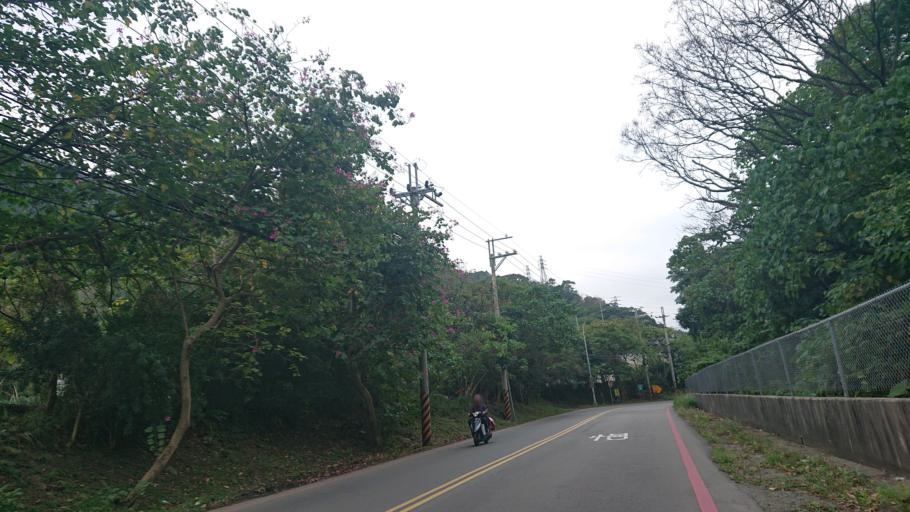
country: TW
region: Taiwan
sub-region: Taoyuan
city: Taoyuan
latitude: 24.9364
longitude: 121.3572
